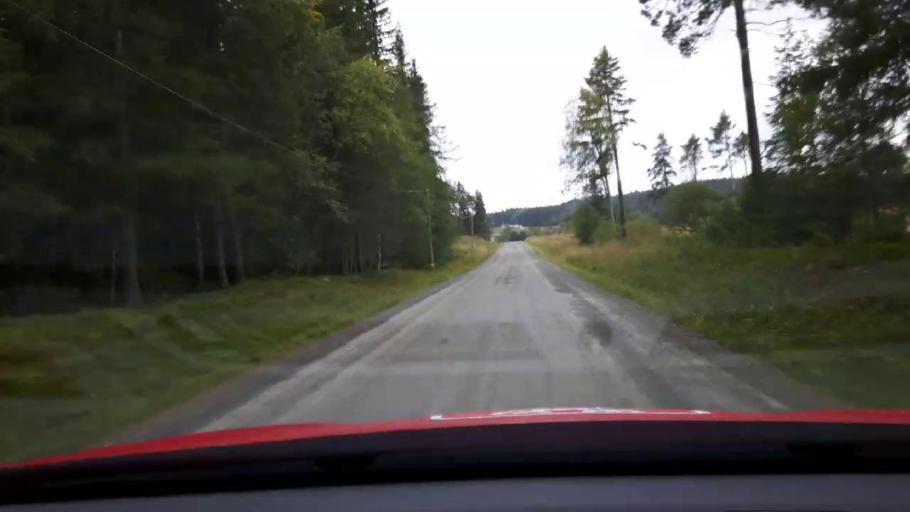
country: SE
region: Jaemtland
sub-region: Bergs Kommun
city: Hoverberg
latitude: 62.8602
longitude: 14.3052
